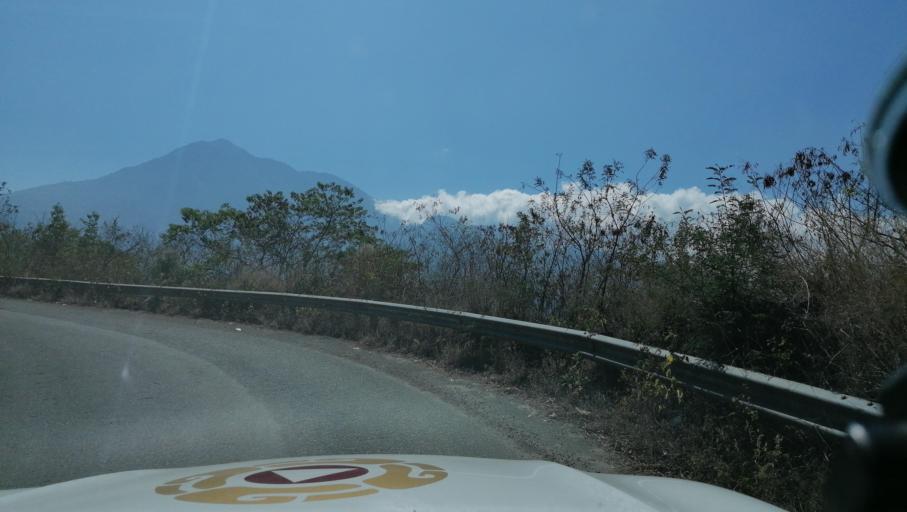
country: MX
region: Chiapas
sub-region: Cacahoatan
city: Benito Juarez
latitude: 15.1846
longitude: -92.1885
